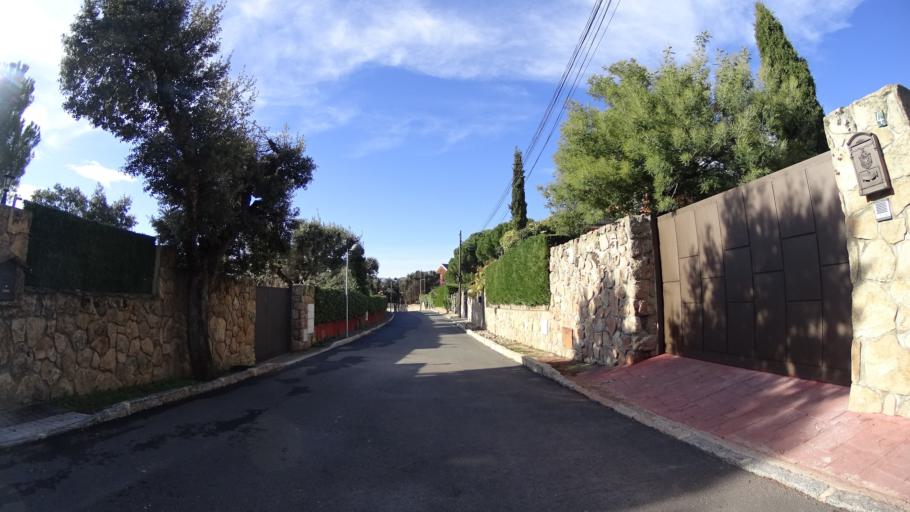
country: ES
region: Madrid
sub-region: Provincia de Madrid
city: Galapagar
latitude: 40.5815
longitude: -4.0236
